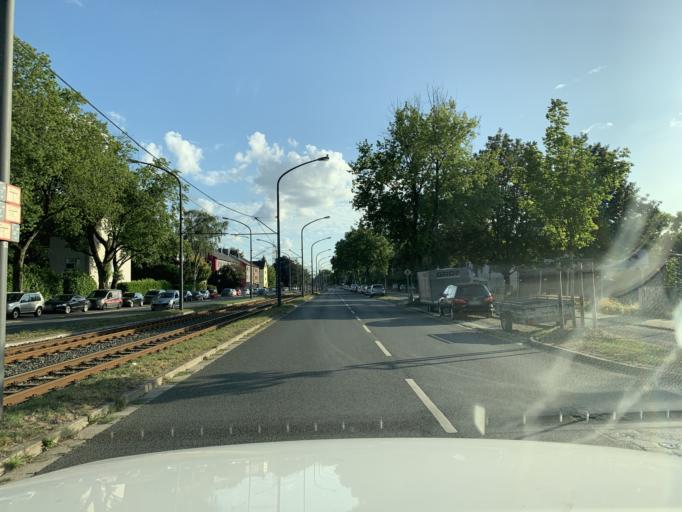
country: DE
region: North Rhine-Westphalia
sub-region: Regierungsbezirk Dusseldorf
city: Oberhausen
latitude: 51.4572
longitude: 6.9246
